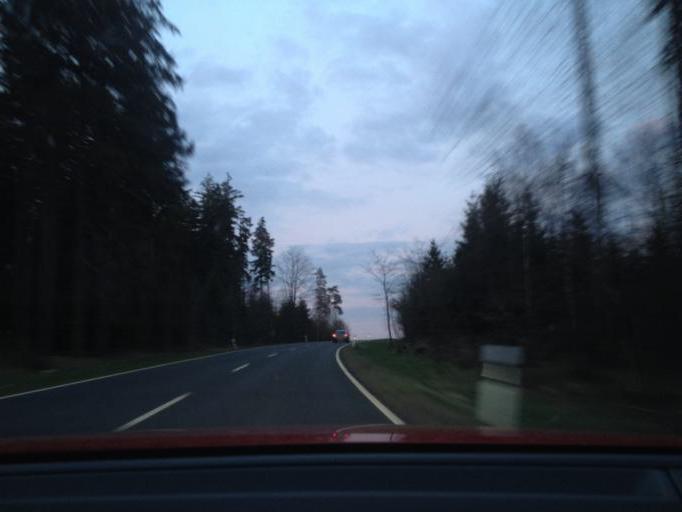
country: DE
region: Bavaria
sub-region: Upper Palatinate
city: Pullenreuth
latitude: 49.9465
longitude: 12.0203
